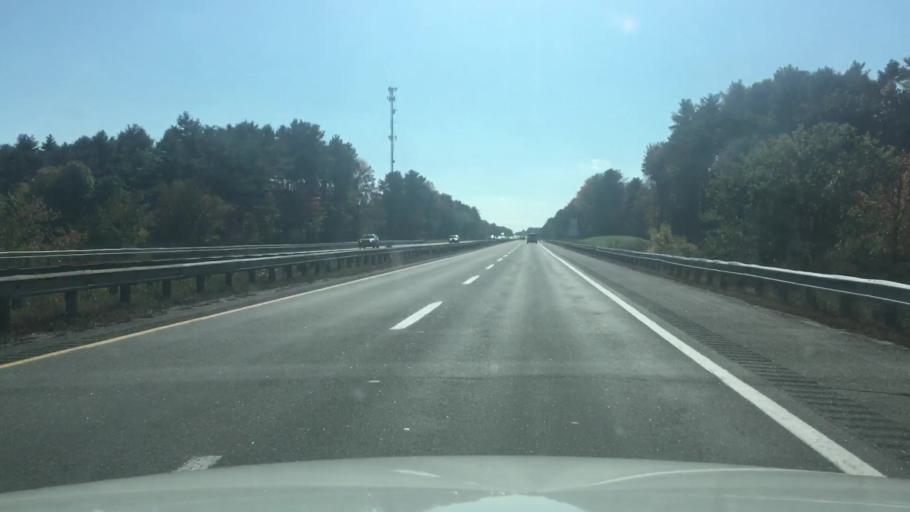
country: US
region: Maine
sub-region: Cumberland County
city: Falmouth
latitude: 43.7103
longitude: -70.3090
